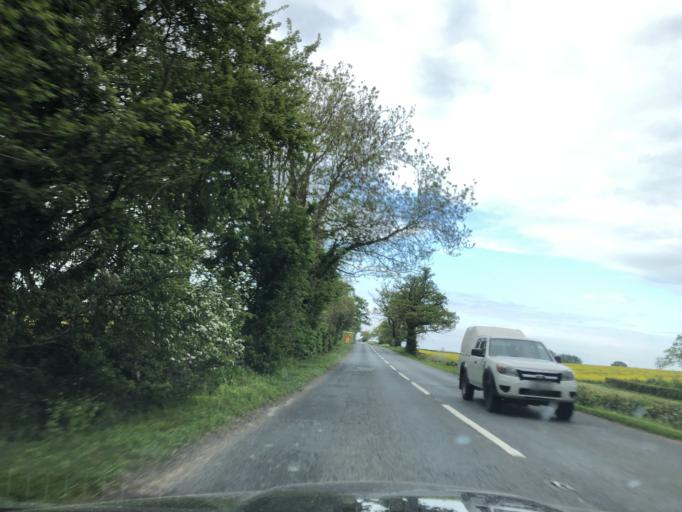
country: GB
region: England
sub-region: Gloucestershire
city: Donnington
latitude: 51.9619
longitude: -1.7116
